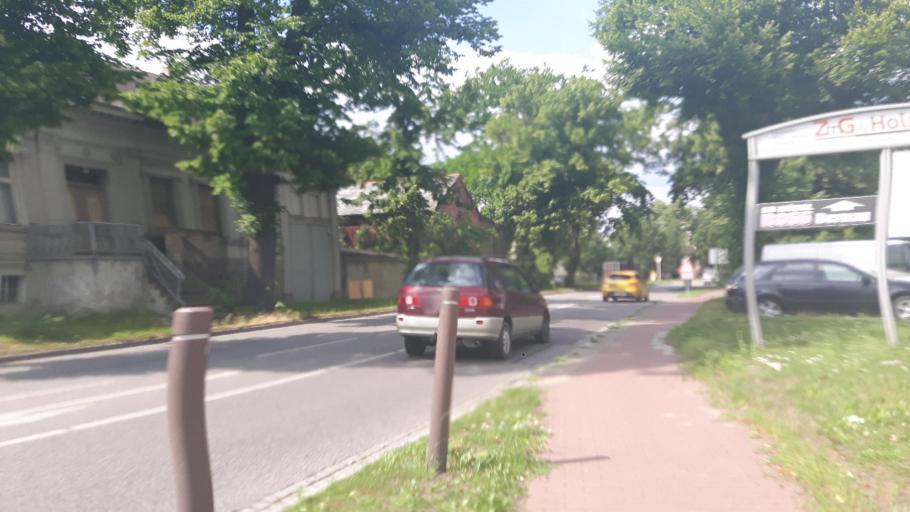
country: DE
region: Berlin
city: Buch
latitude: 52.6257
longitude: 13.5441
